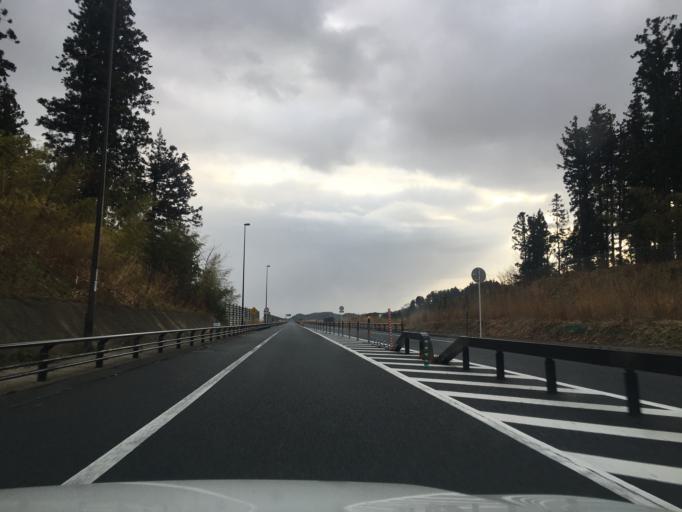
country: JP
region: Yamagata
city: Tsuruoka
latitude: 38.7081
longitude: 139.7356
